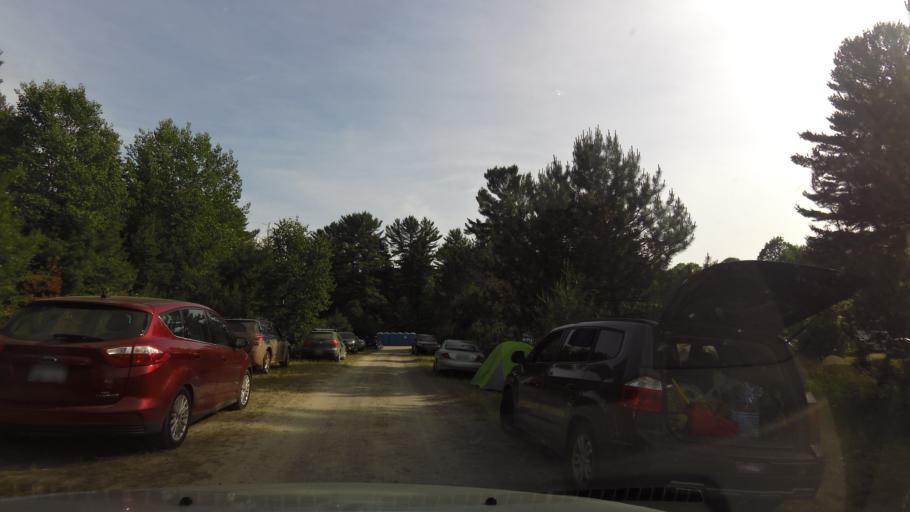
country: CA
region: Ontario
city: Greater Sudbury
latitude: 45.9094
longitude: -80.5547
